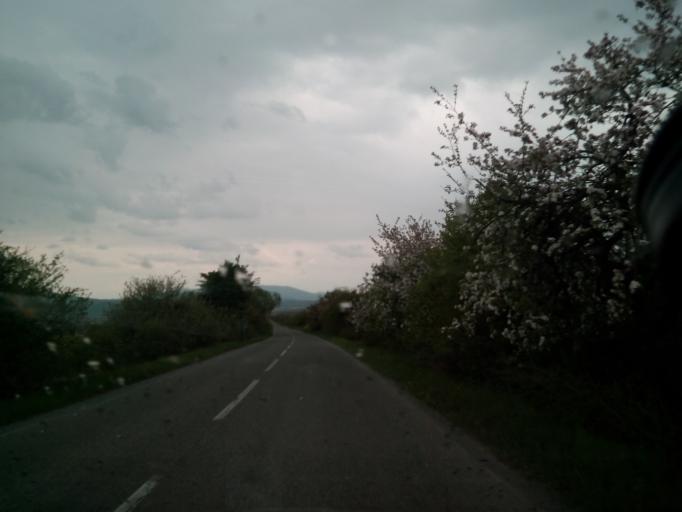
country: SK
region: Kosicky
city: Secovce
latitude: 48.7898
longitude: 21.4803
